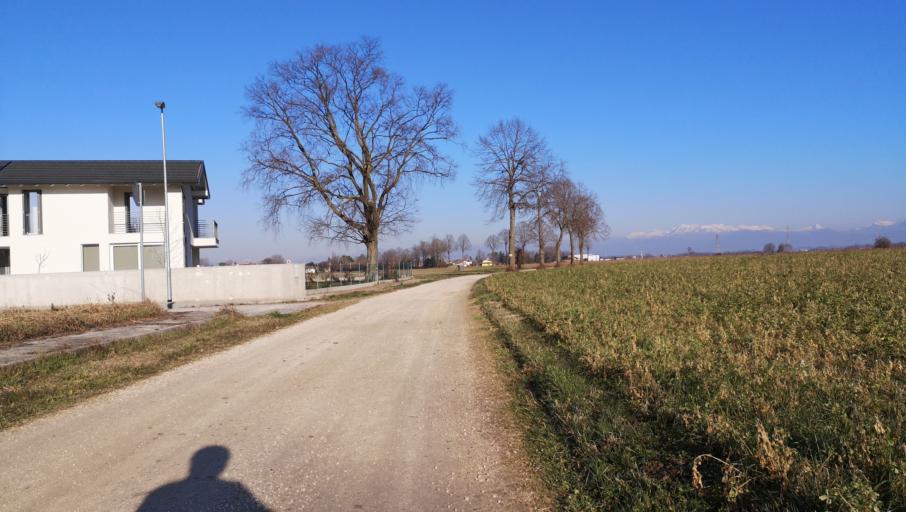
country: IT
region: Friuli Venezia Giulia
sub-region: Provincia di Udine
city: Palmanova
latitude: 45.9145
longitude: 13.2991
